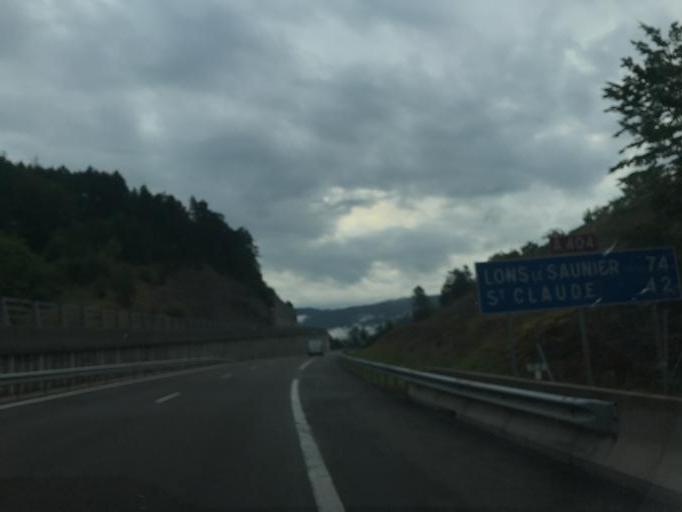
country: FR
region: Rhone-Alpes
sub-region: Departement de l'Ain
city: Montreal-la-Cluse
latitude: 46.1885
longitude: 5.5685
